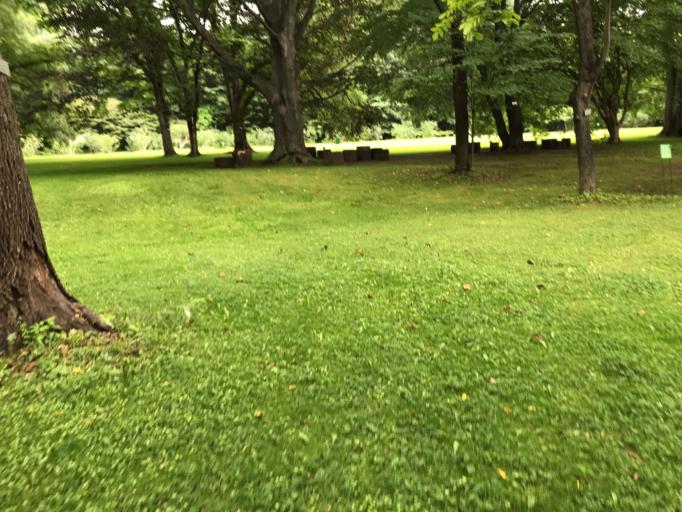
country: JP
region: Hokkaido
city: Sapporo
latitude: 43.0646
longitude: 141.3421
